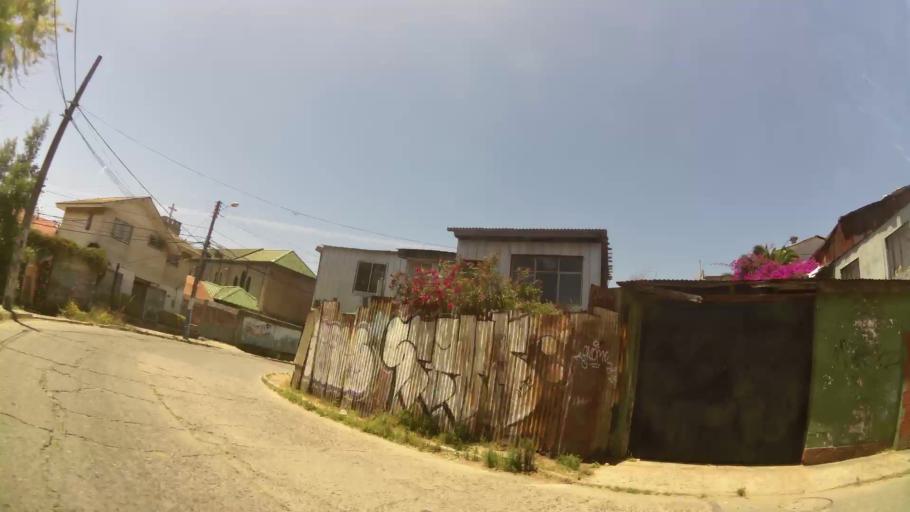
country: CL
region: Valparaiso
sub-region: Provincia de Valparaiso
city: Valparaiso
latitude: -33.0419
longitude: -71.6355
